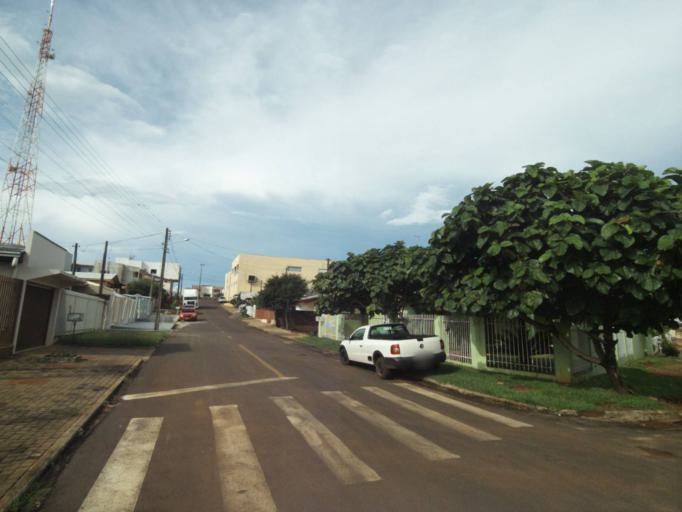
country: BR
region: Parana
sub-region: Guaraniacu
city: Guaraniacu
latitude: -25.1034
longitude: -52.8662
